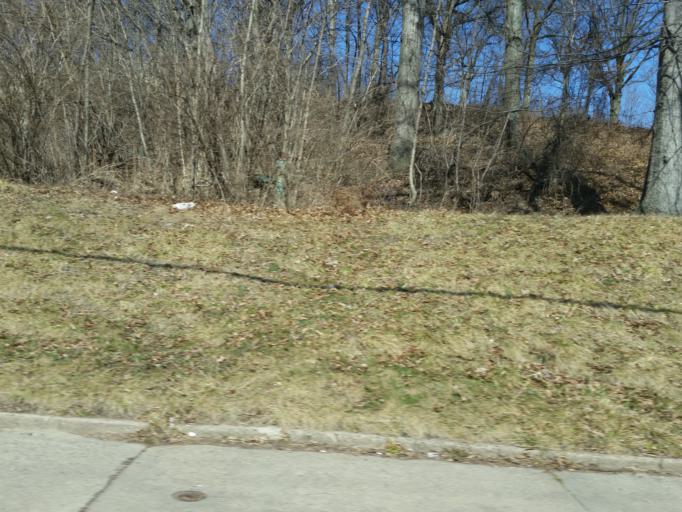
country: US
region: Pennsylvania
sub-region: Allegheny County
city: McKees Rocks
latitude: 40.4649
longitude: -80.0704
